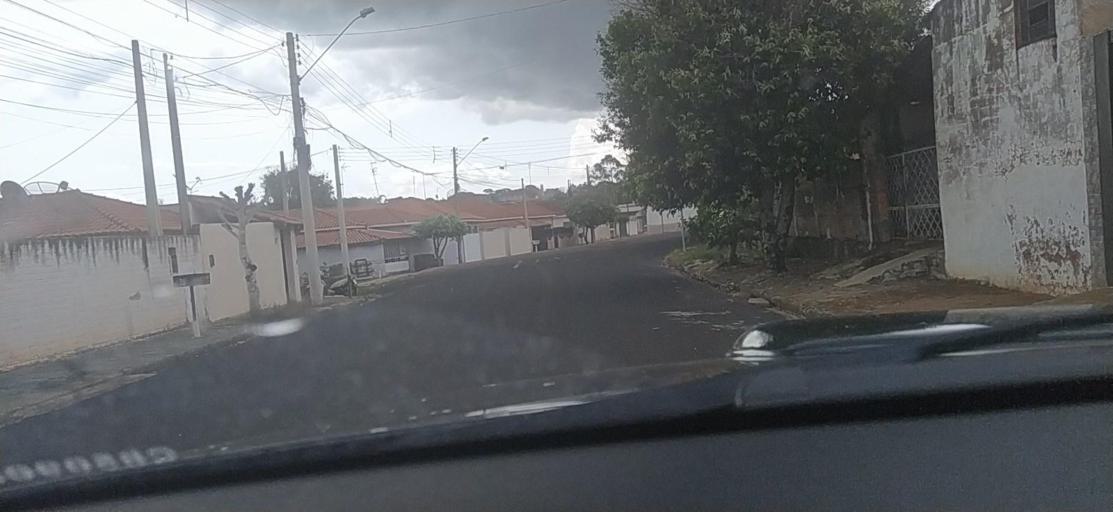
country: BR
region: Sao Paulo
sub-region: Pindorama
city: Pindorama
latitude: -21.1918
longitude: -48.9031
